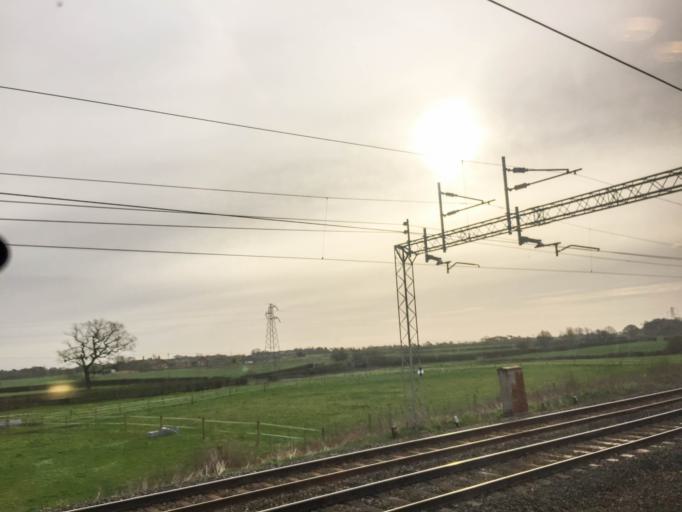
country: GB
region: England
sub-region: Cheshire West and Chester
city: Winsford
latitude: 53.1794
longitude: -2.4841
